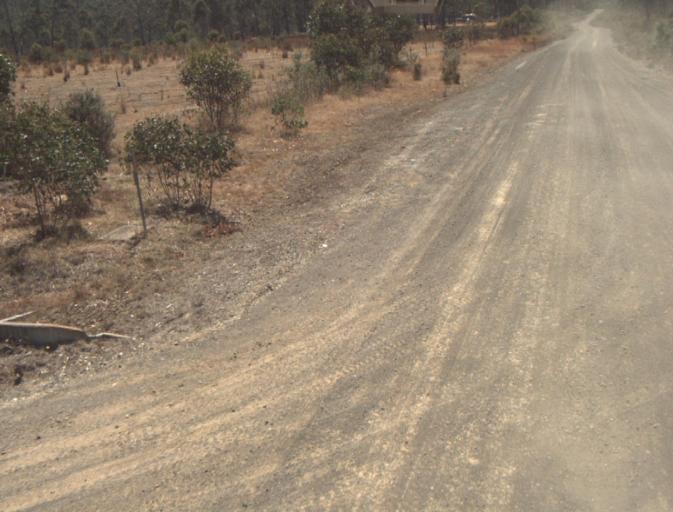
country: AU
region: Tasmania
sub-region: Launceston
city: Mayfield
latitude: -41.2772
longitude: 147.0985
